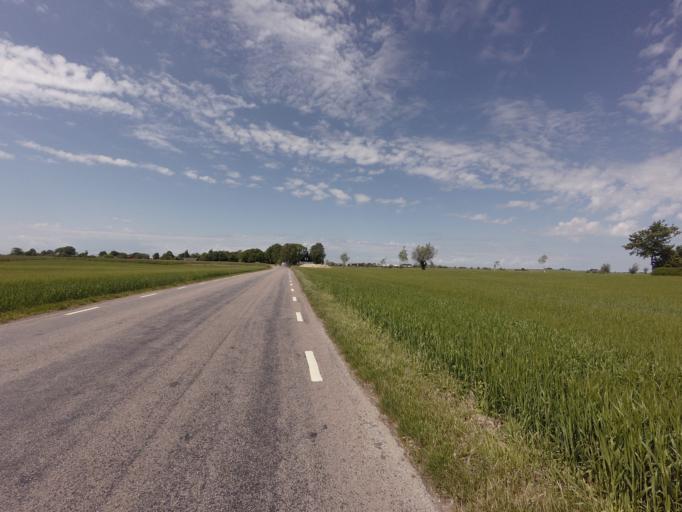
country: SE
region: Skane
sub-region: Trelleborgs Kommun
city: Skare
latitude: 55.4248
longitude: 13.0919
